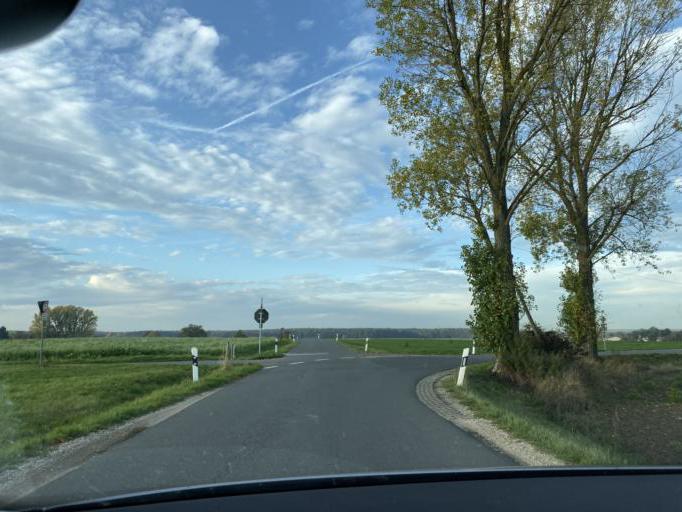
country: DE
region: Bavaria
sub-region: Regierungsbezirk Mittelfranken
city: Puschendorf
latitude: 49.5411
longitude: 10.8370
